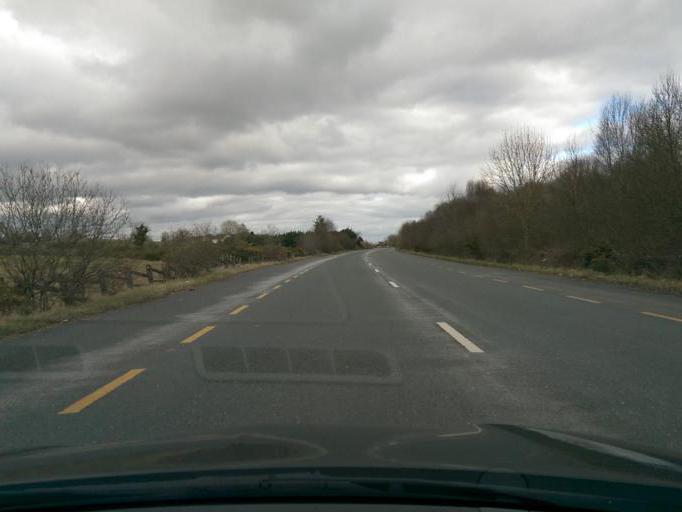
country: IE
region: Connaught
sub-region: County Galway
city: Ballinasloe
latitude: 53.3378
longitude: -8.1248
